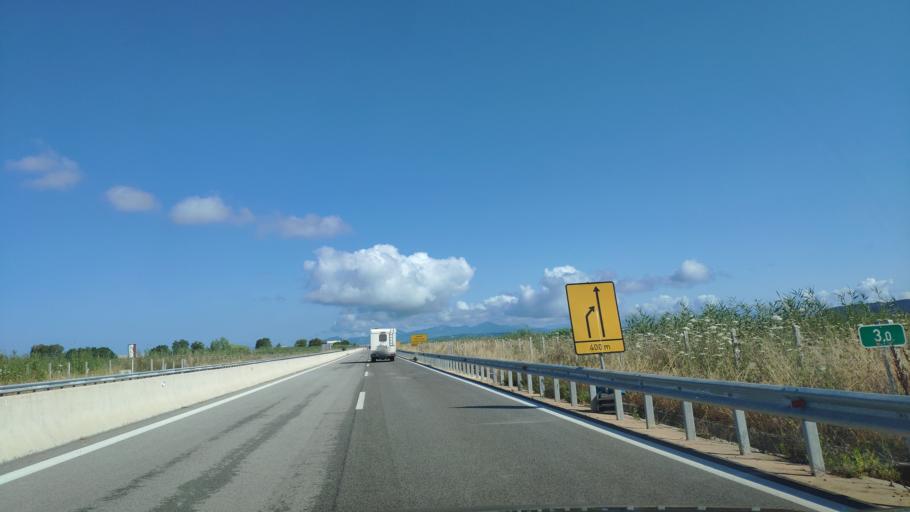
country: GR
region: Epirus
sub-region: Nomos Prevezis
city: Preveza
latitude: 38.9214
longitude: 20.7882
